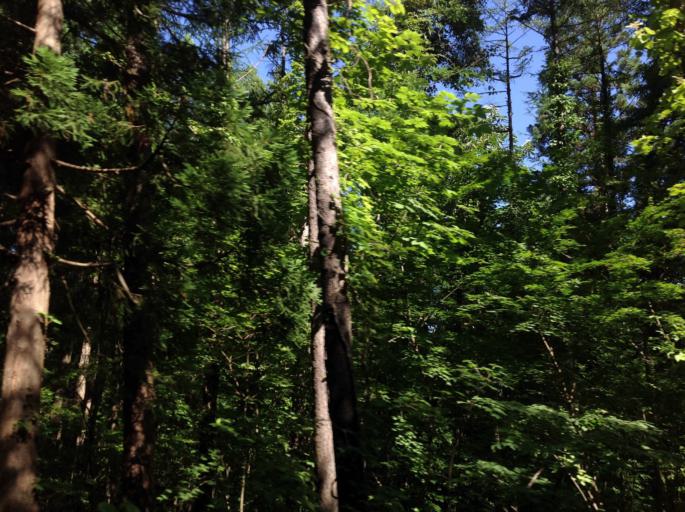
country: JP
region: Akita
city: Kakunodatemachi
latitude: 39.6982
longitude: 140.6686
